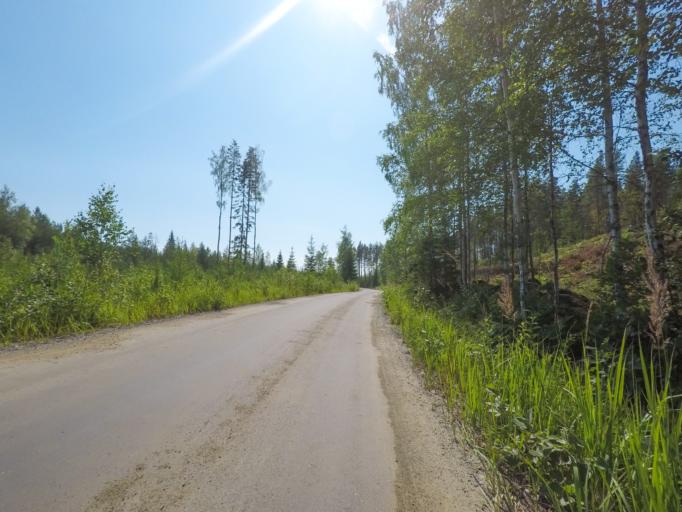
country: FI
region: Southern Savonia
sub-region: Mikkeli
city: Puumala
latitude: 61.4087
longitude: 28.0473
